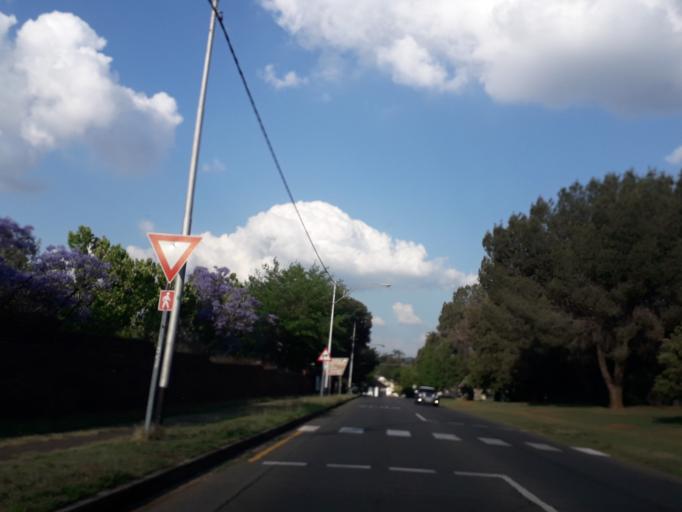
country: ZA
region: Gauteng
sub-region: City of Johannesburg Metropolitan Municipality
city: Johannesburg
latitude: -26.1513
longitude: 28.0002
